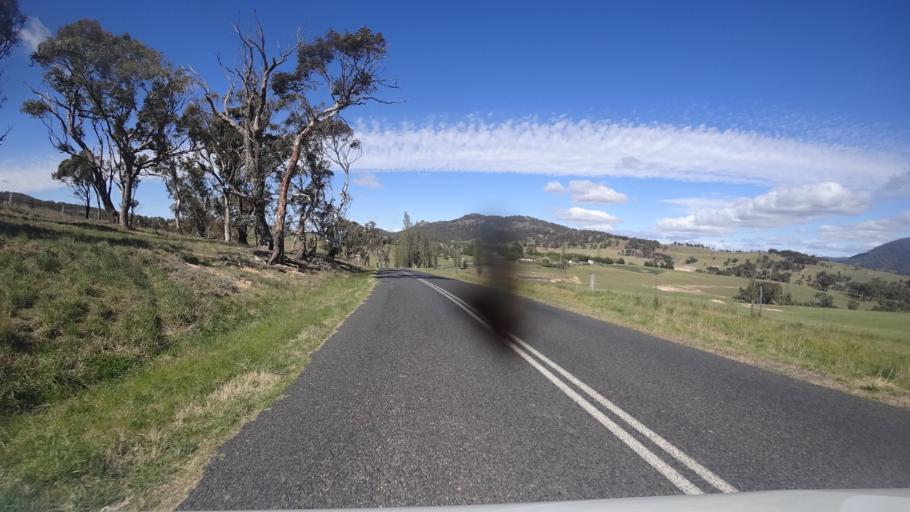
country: AU
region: New South Wales
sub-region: Lithgow
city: Portland
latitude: -33.5206
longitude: 149.9461
